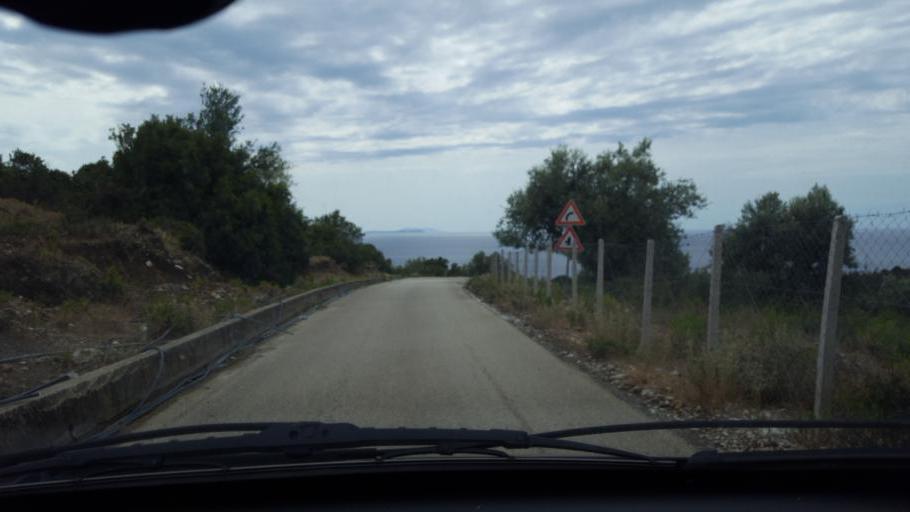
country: AL
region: Vlore
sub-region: Rrethi i Sarandes
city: Lukove
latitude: 39.9749
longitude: 19.9198
